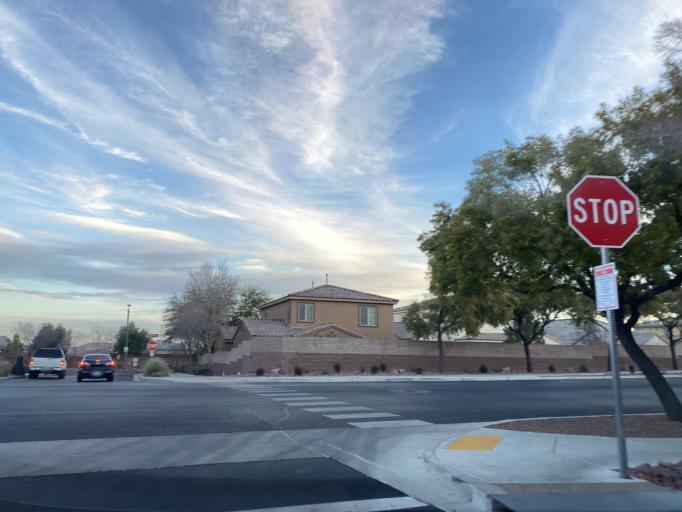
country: US
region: Nevada
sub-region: Clark County
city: Summerlin South
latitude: 36.3012
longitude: -115.3239
